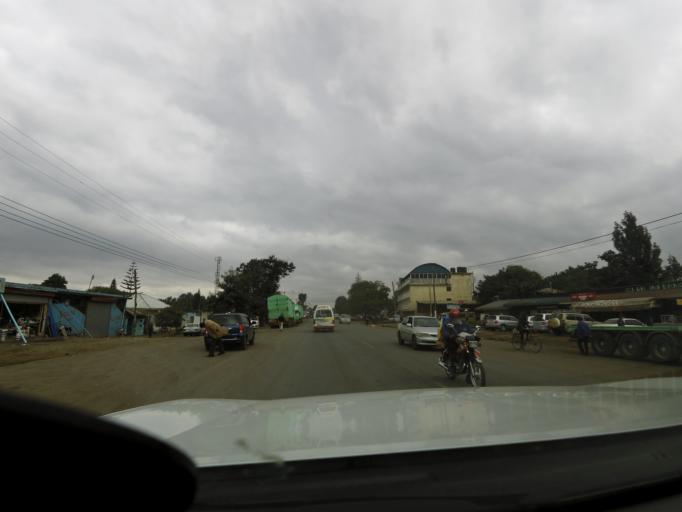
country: TZ
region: Arusha
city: Arusha
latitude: -3.3630
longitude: 36.6724
